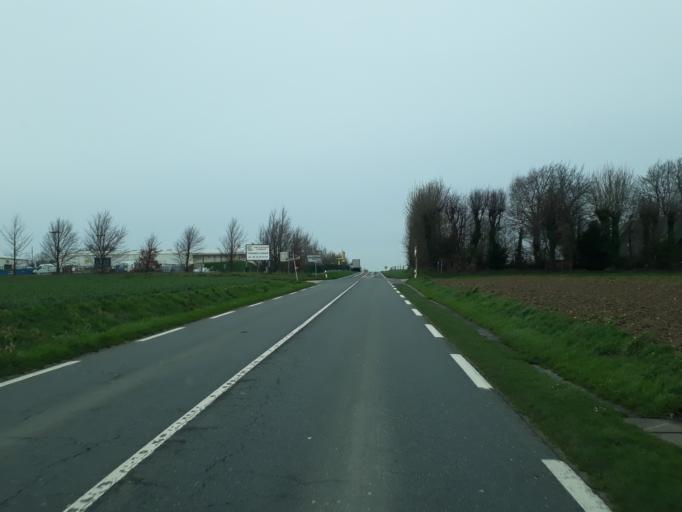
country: FR
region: Haute-Normandie
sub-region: Departement de la Seine-Maritime
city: Beuzeville-la-Grenier
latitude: 49.6046
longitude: 0.4151
